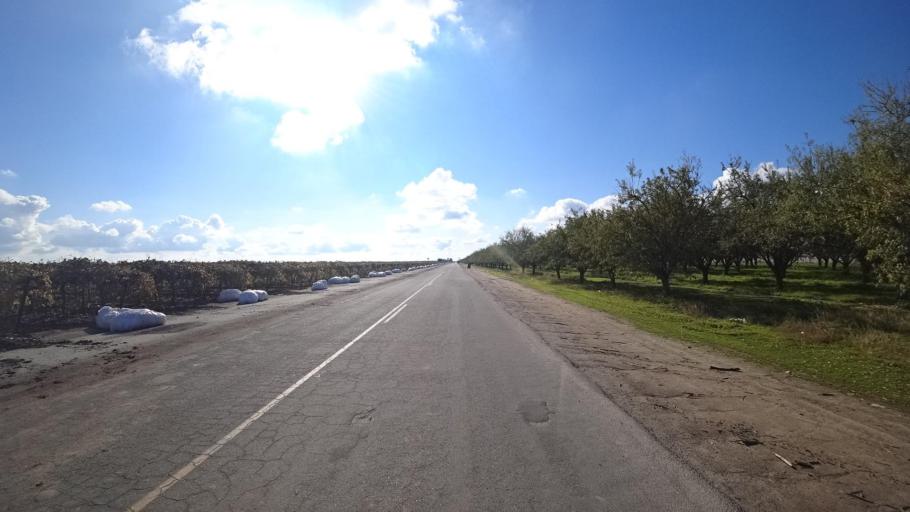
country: US
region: California
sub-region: Kern County
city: McFarland
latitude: 35.6812
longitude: -119.2587
